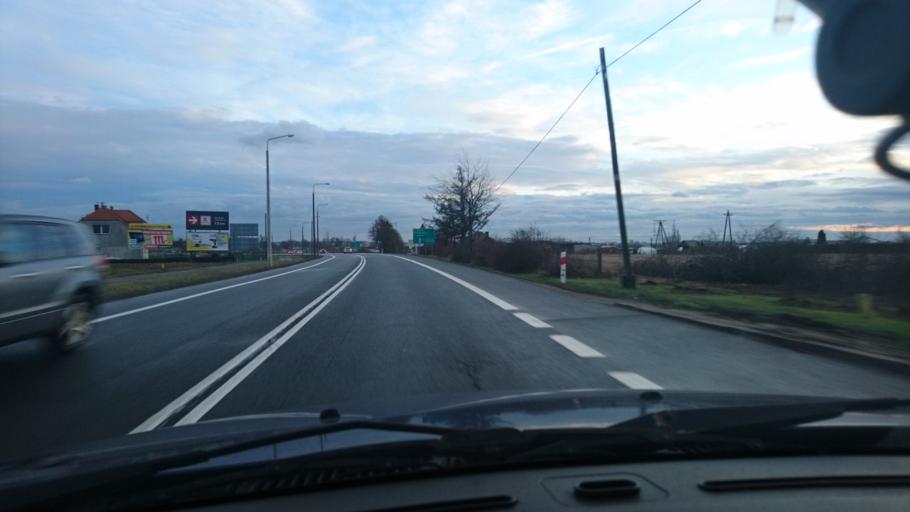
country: PL
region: Opole Voivodeship
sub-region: Powiat kluczborski
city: Kluczbork
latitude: 50.9954
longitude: 18.2087
